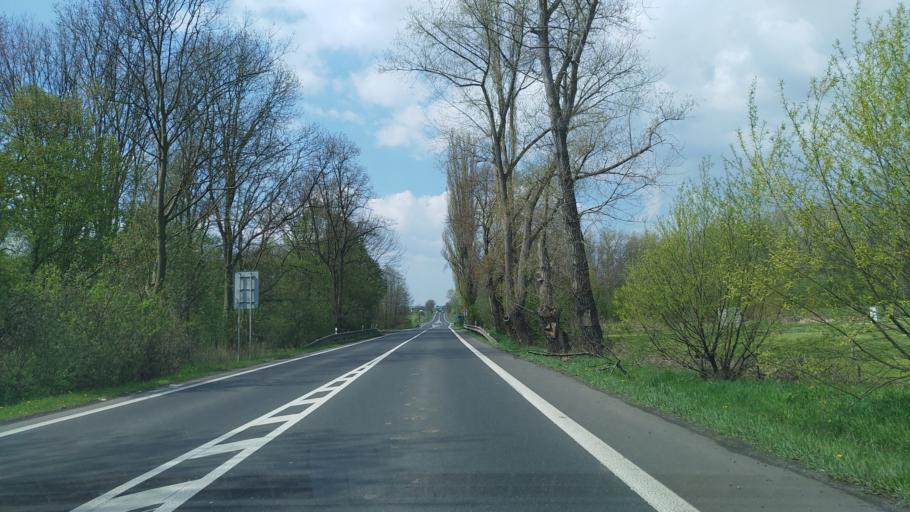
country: CZ
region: Ustecky
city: Krupka
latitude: 50.6667
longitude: 13.8828
